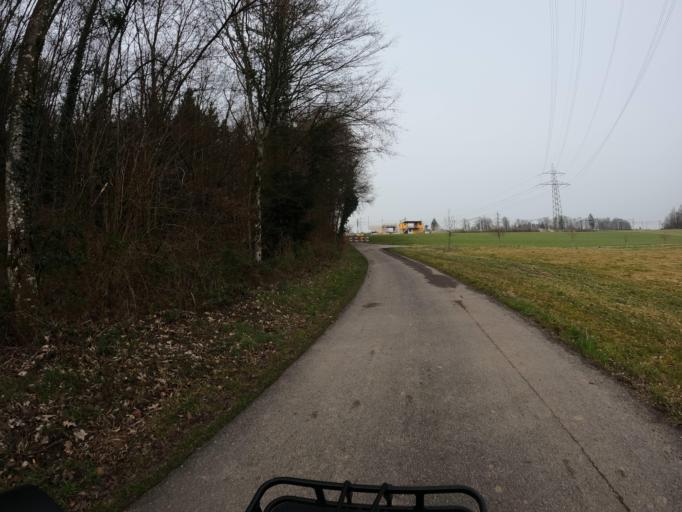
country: CH
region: Aargau
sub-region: Bezirk Baden
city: Mellingen
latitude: 47.4184
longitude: 8.2463
